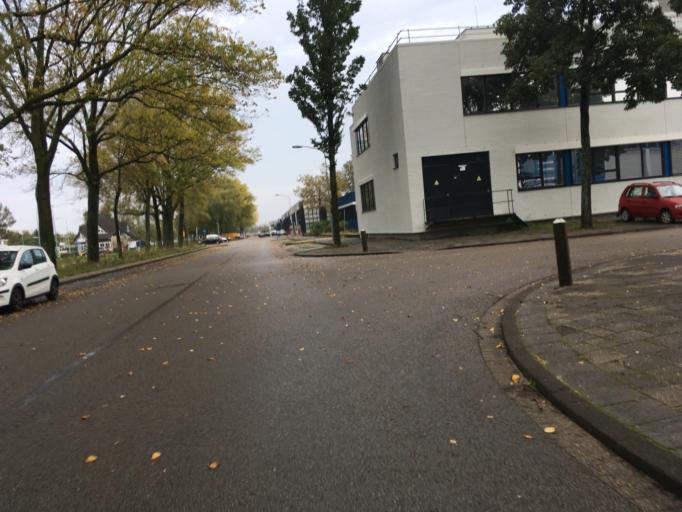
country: NL
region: North Holland
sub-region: Gemeente Haarlem
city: Haarlem
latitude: 52.3897
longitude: 4.6639
